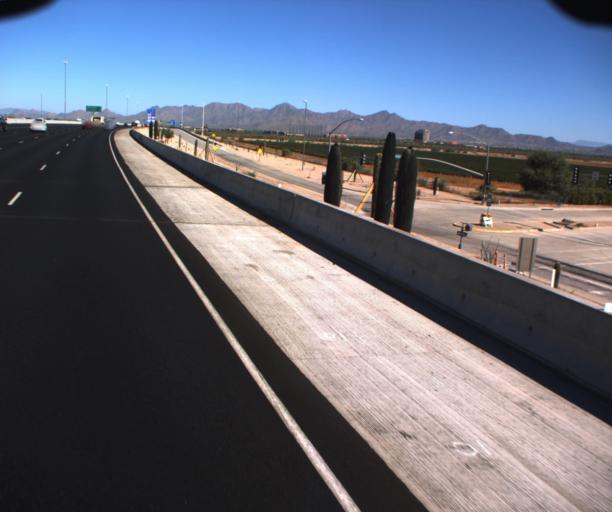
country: US
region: Arizona
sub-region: Maricopa County
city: Scottsdale
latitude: 33.5235
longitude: -111.8873
